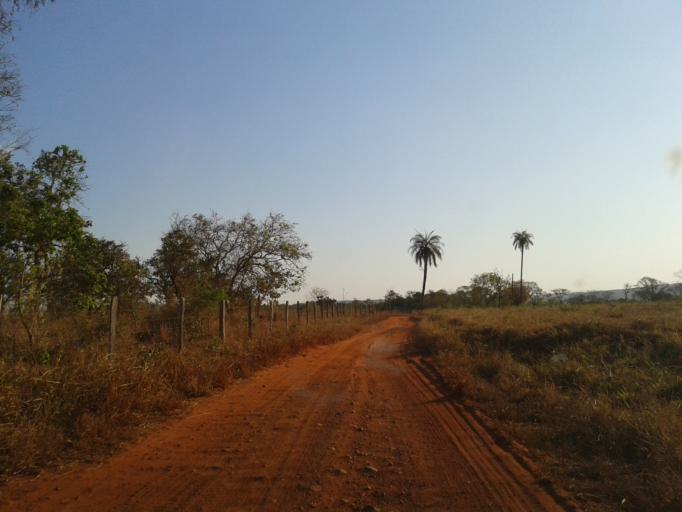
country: BR
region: Minas Gerais
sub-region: Ituiutaba
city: Ituiutaba
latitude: -19.2437
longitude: -49.5962
